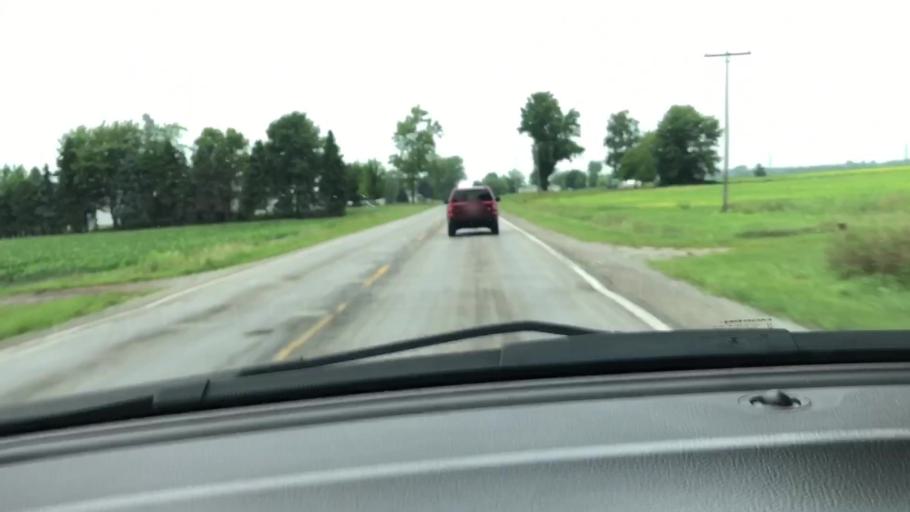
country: US
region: Michigan
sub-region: Saginaw County
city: Freeland
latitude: 43.5463
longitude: -84.0902
